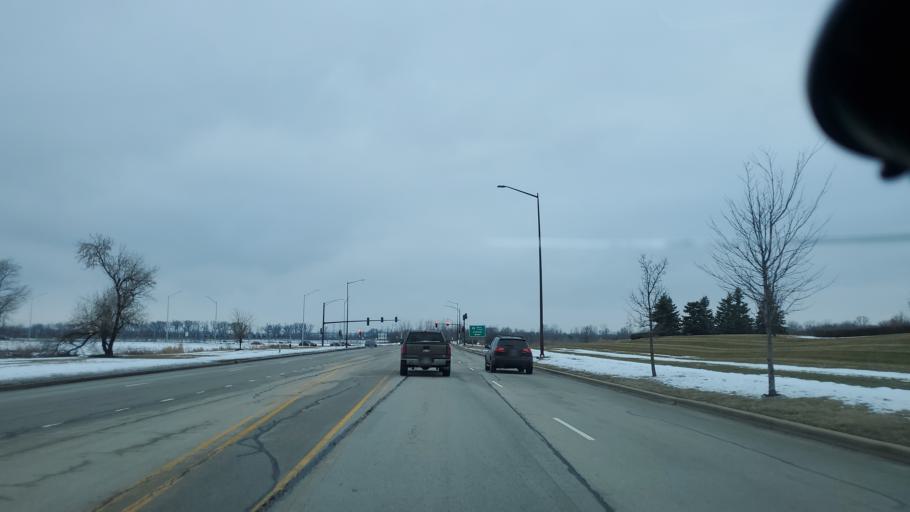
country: US
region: Illinois
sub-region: DuPage County
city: Warrenville
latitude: 41.8067
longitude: -88.2440
